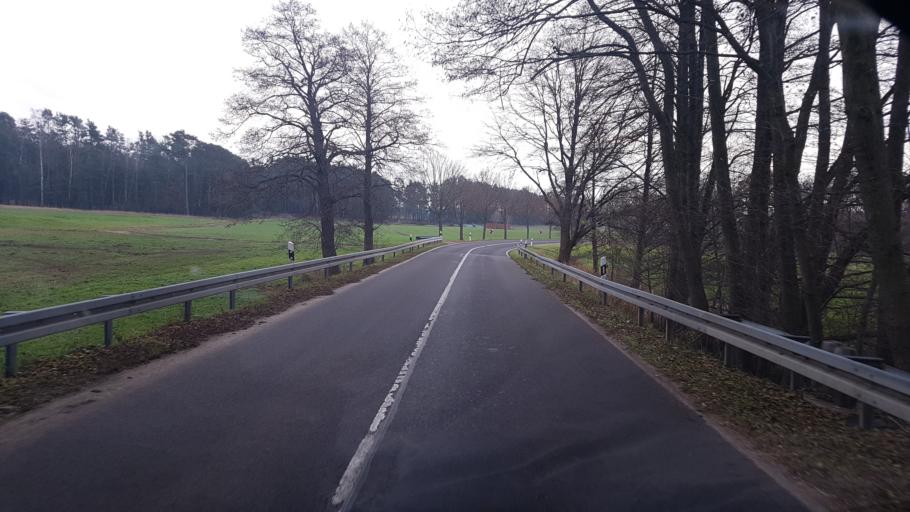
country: DE
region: Brandenburg
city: Schenkendobern
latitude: 51.9424
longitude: 14.6323
